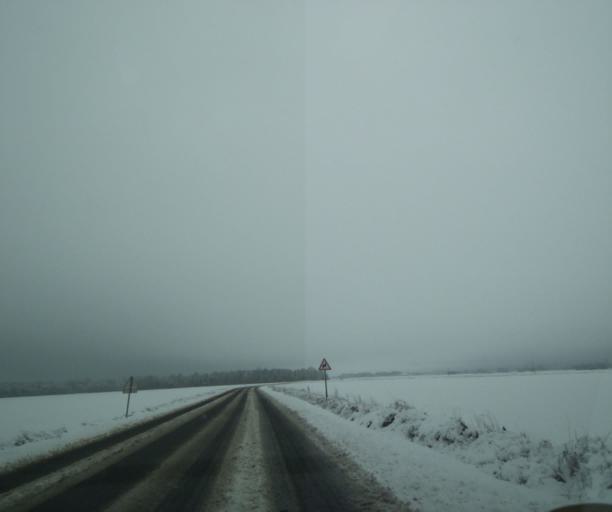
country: FR
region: Champagne-Ardenne
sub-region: Departement de la Haute-Marne
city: Saint-Dizier
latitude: 48.5669
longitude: 4.9206
